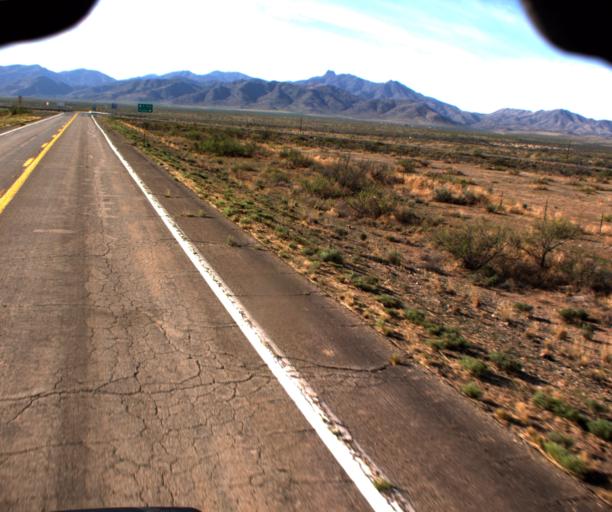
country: US
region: Arizona
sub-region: Cochise County
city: Willcox
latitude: 32.3649
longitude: -109.6224
